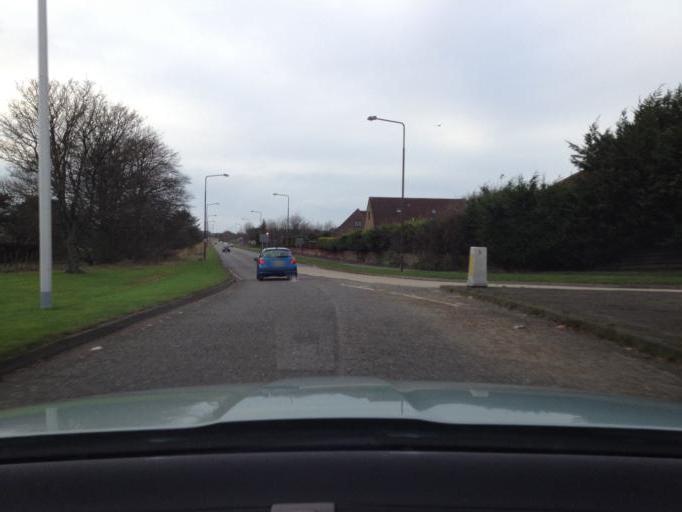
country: GB
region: Scotland
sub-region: West Lothian
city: Broxburn
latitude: 55.9340
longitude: -3.4508
